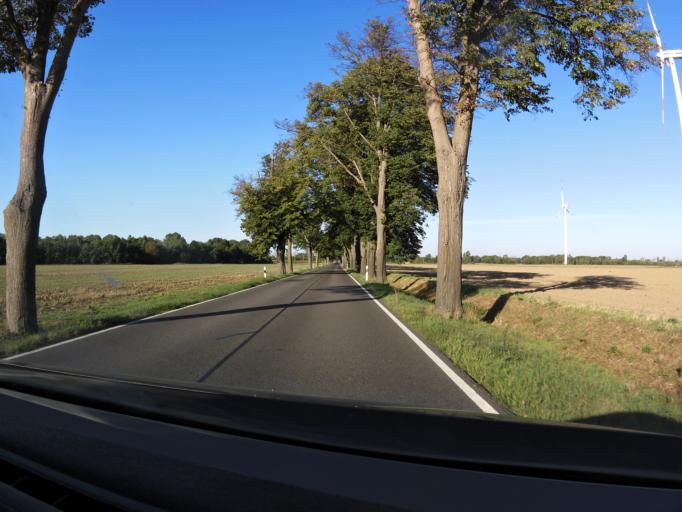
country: DE
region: Mecklenburg-Vorpommern
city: Alt-Sanitz
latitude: 53.8301
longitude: 13.5505
